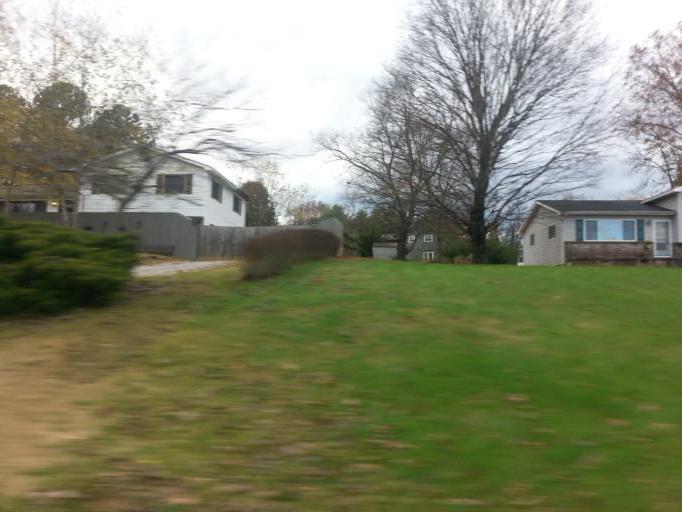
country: US
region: Tennessee
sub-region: Knox County
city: Knoxville
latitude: 35.9459
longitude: -84.0044
